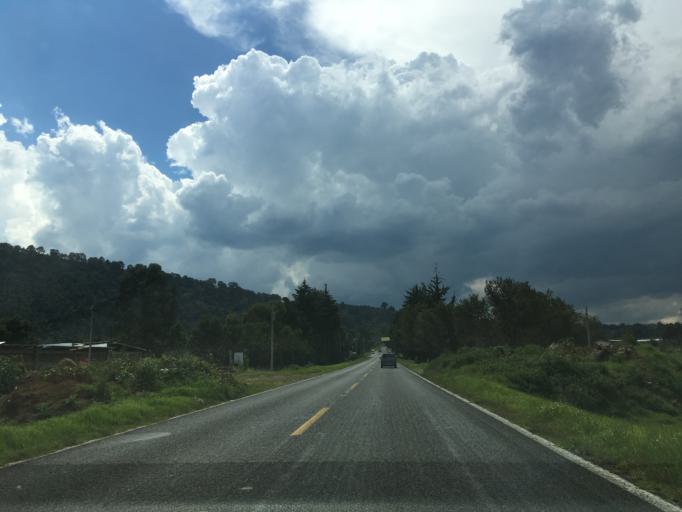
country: MX
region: Michoacan
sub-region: Patzcuaro
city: Santa Ana Chapitiro
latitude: 19.5266
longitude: -101.6449
